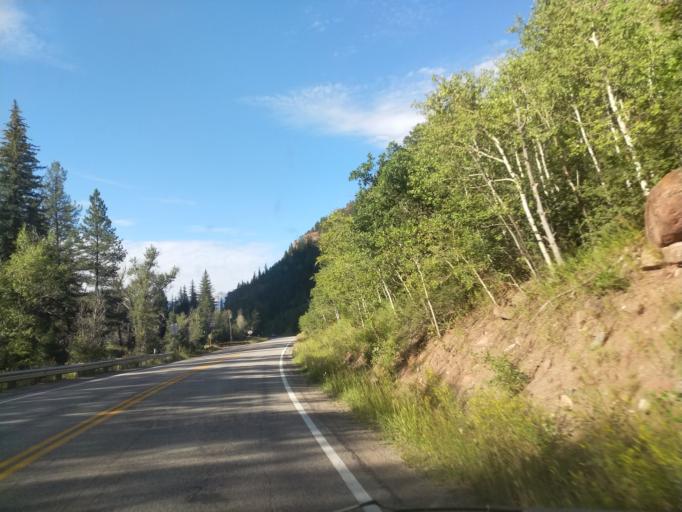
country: US
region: Colorado
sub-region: Garfield County
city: Carbondale
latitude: 39.2030
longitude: -107.2316
